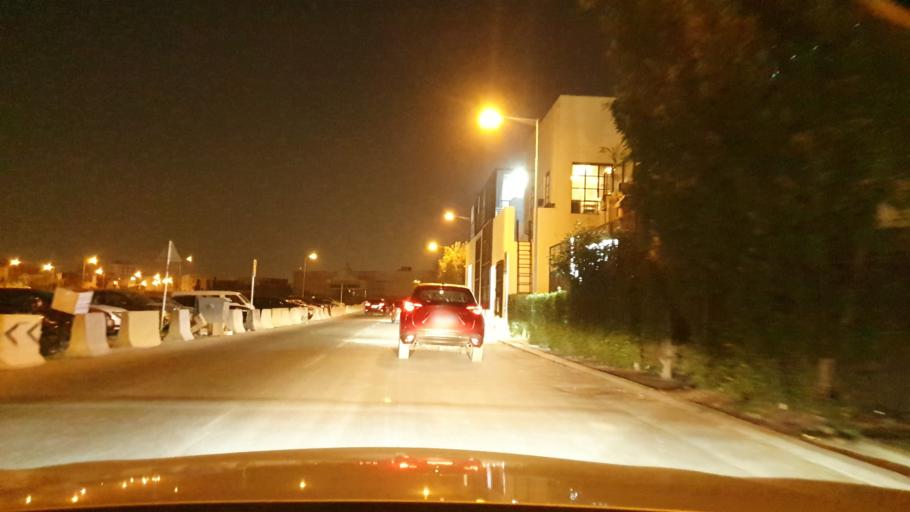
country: BH
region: Manama
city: Jidd Hafs
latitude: 26.1972
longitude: 50.4777
